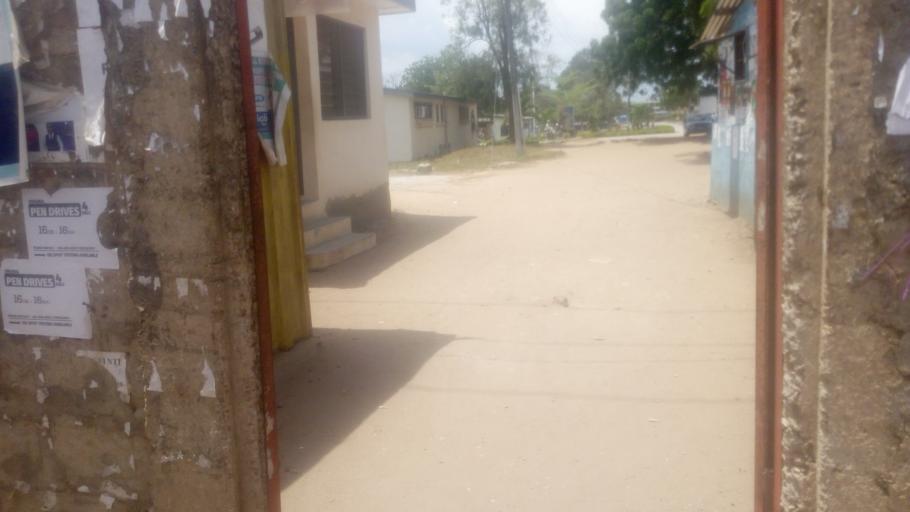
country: GH
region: Central
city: Winneba
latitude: 5.3608
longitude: -0.6310
